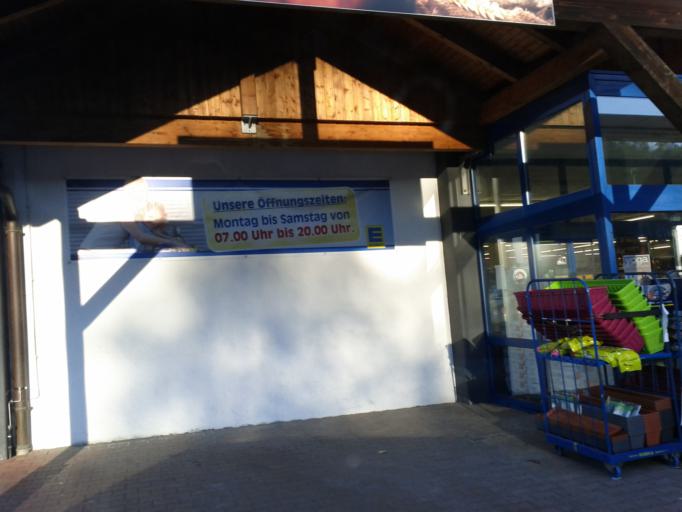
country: DE
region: Bavaria
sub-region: Upper Franconia
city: Weismain
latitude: 50.0915
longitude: 11.2390
